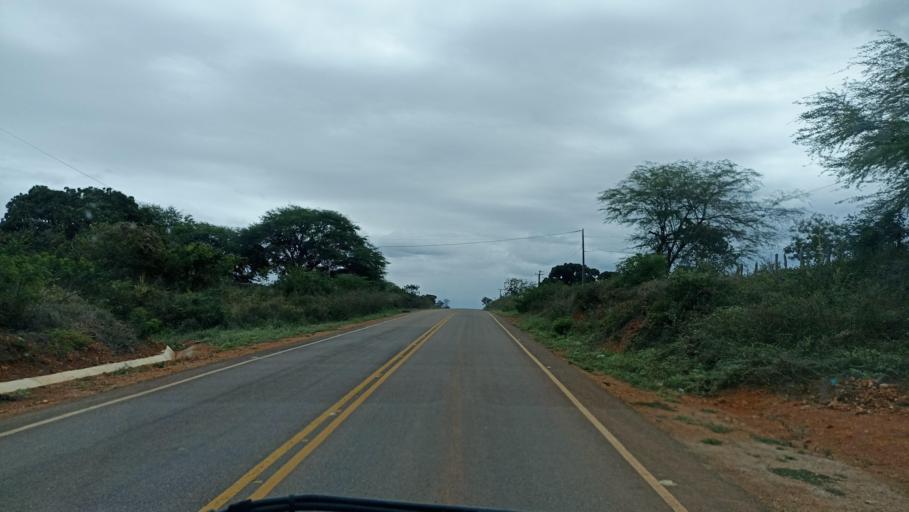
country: BR
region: Bahia
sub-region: Andarai
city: Vera Cruz
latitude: -12.9909
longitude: -41.0021
